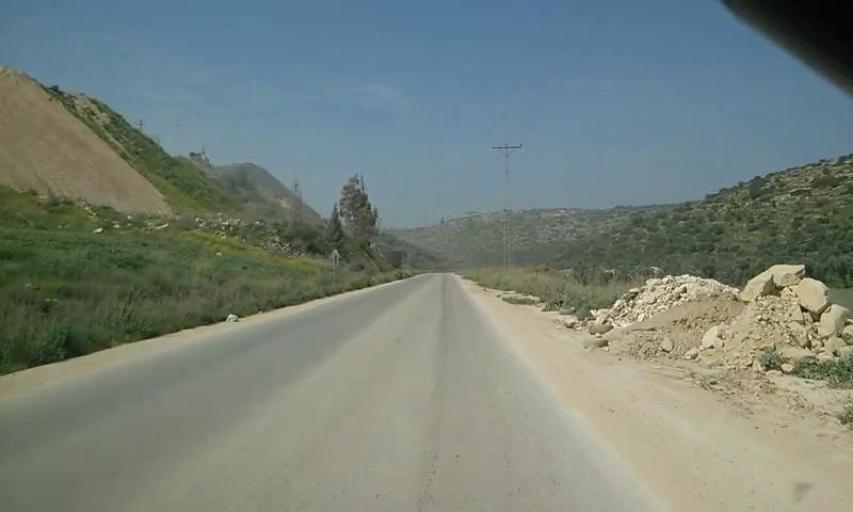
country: PS
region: West Bank
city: Az Zababidah
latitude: 32.4047
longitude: 35.3151
